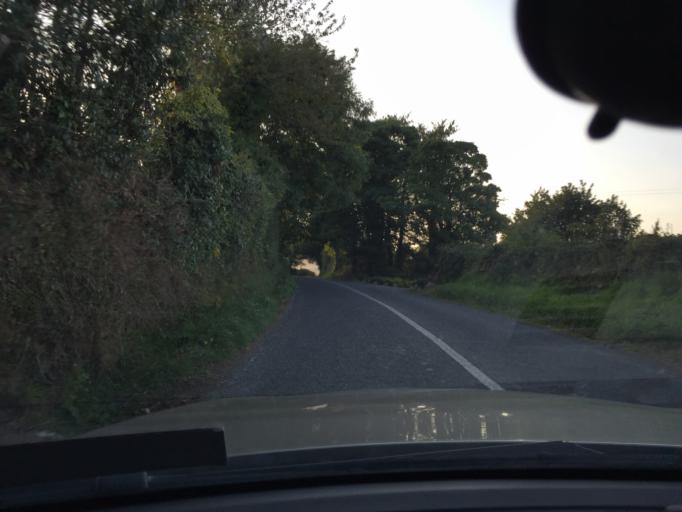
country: IE
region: Leinster
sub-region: Wicklow
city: Enniskerry
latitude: 53.1673
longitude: -6.1763
